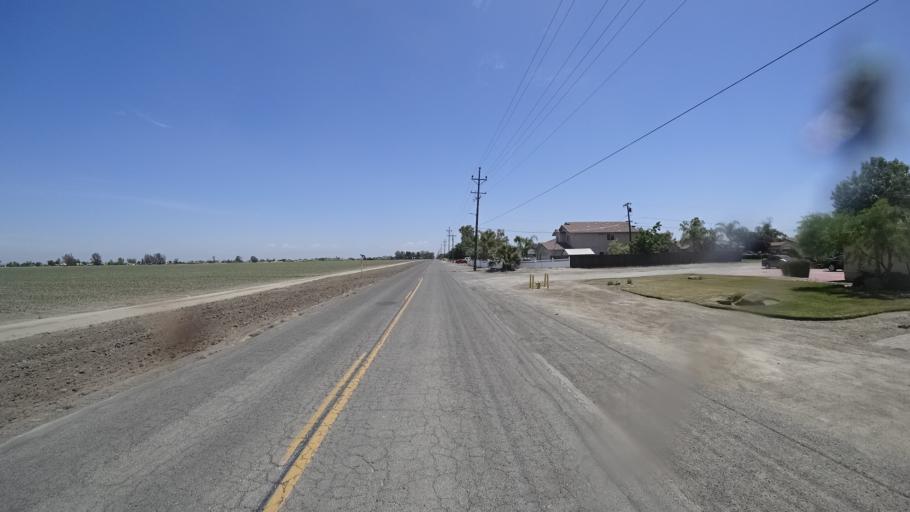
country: US
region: California
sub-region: Kings County
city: Corcoran
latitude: 36.1090
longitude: -119.5883
